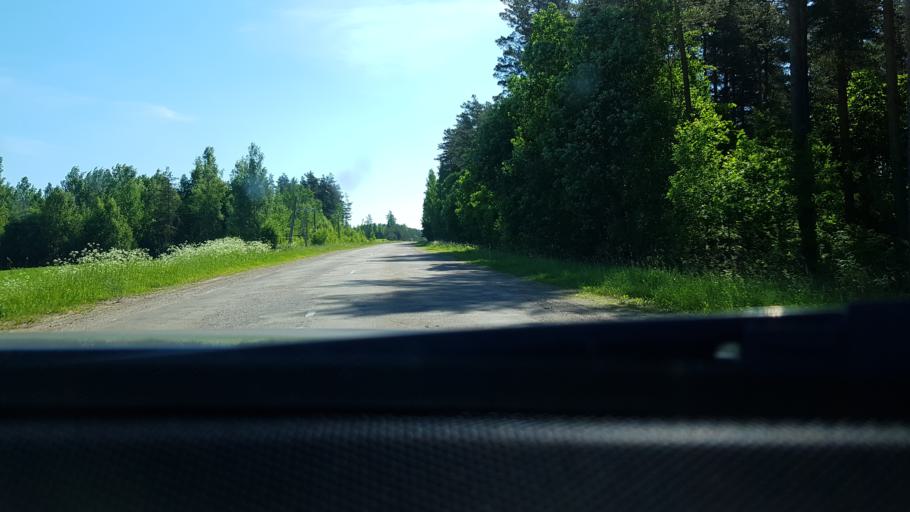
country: LV
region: Kraslavas Rajons
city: Kraslava
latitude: 55.8631
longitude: 26.9840
